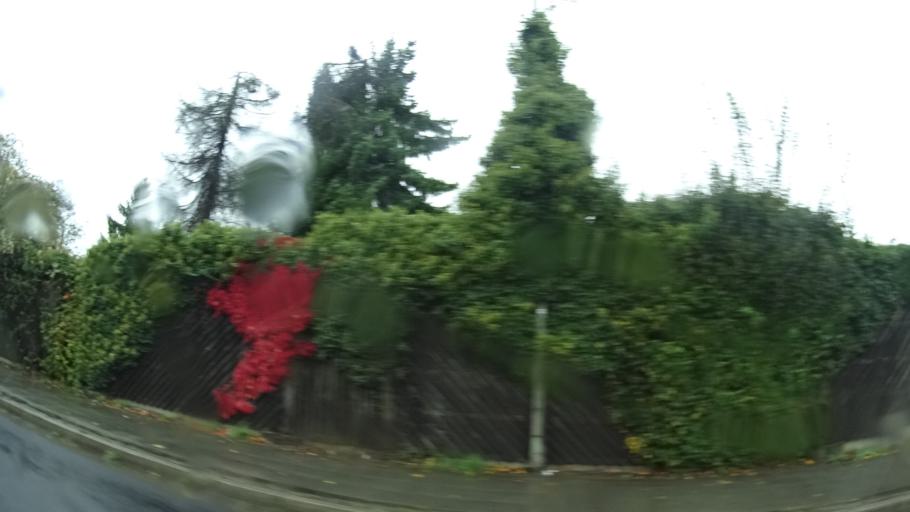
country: DE
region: Bavaria
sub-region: Upper Franconia
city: Kronach
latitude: 50.2304
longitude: 11.3222
